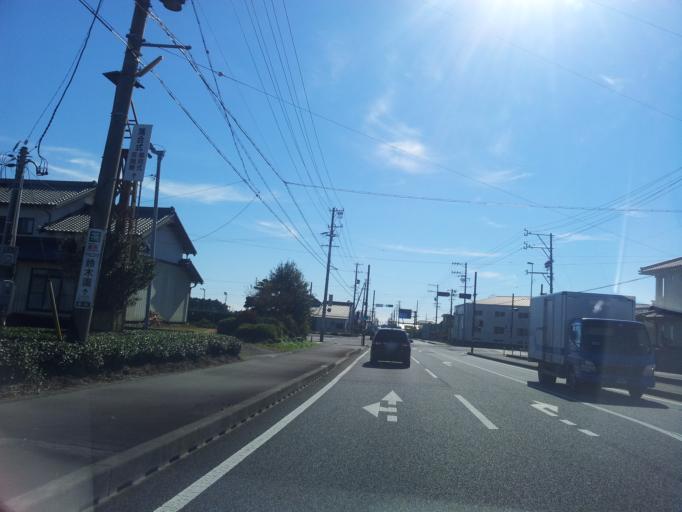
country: JP
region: Shizuoka
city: Kanaya
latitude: 34.8039
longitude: 138.1352
